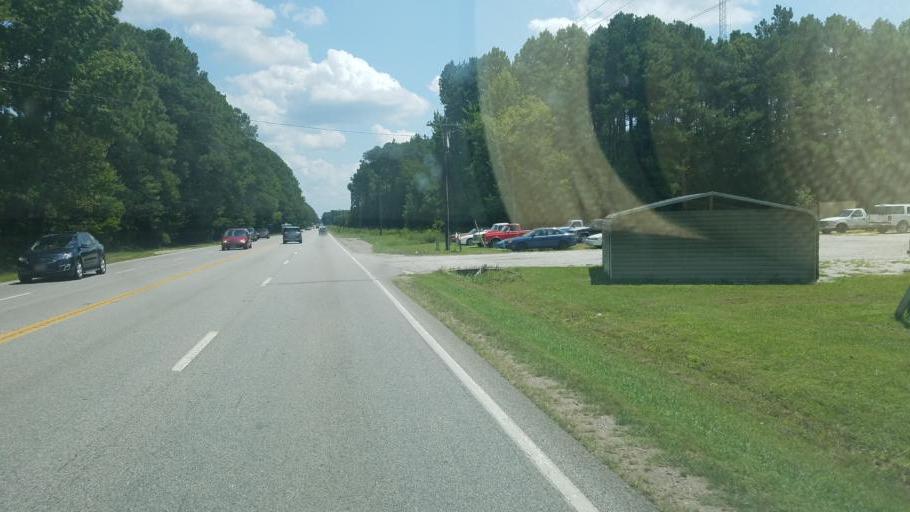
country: US
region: Virginia
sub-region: Sussex County
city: Waverly
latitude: 37.0607
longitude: -77.1290
